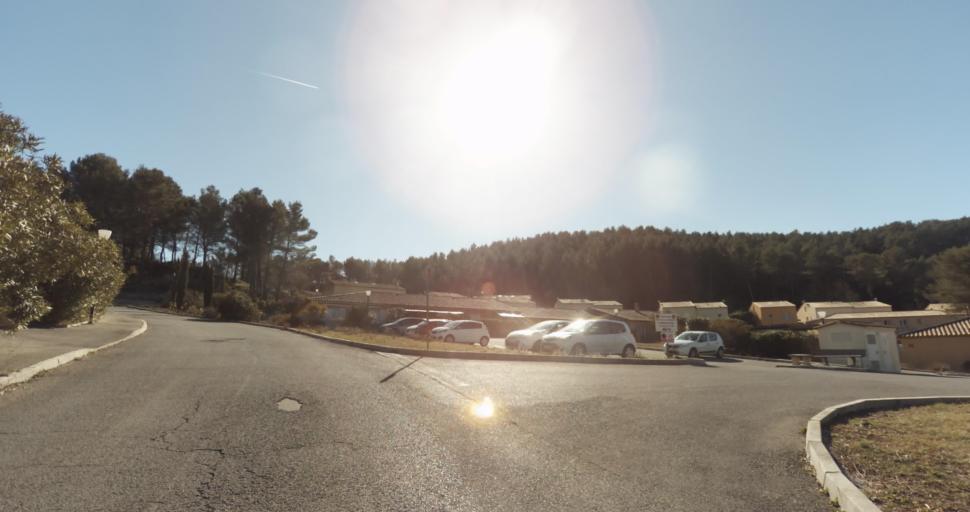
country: FR
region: Provence-Alpes-Cote d'Azur
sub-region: Departement des Bouches-du-Rhone
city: Peypin
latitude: 43.3918
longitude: 5.5748
